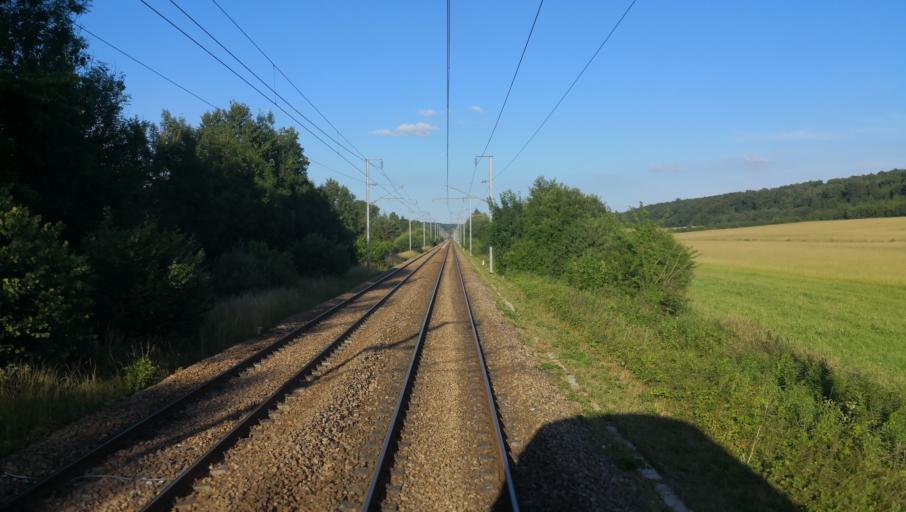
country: FR
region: Haute-Normandie
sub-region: Departement de l'Eure
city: Saint-Sebastien-de-Morsent
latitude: 48.9944
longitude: 1.0679
